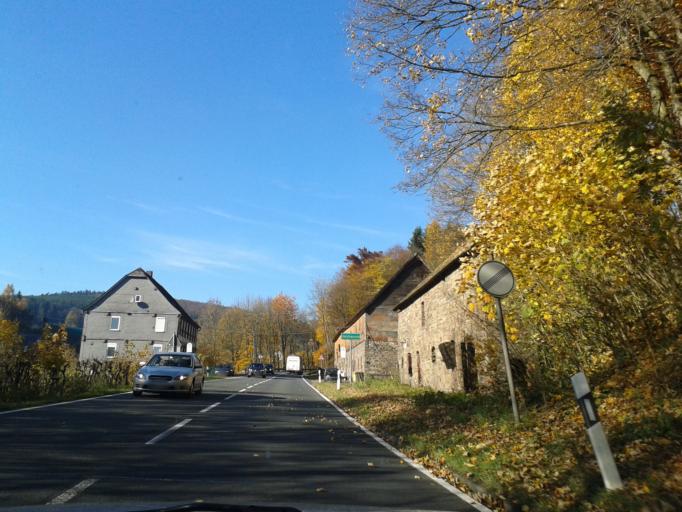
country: DE
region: North Rhine-Westphalia
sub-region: Regierungsbezirk Arnsberg
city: Bad Laasphe
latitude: 50.9614
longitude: 8.3498
